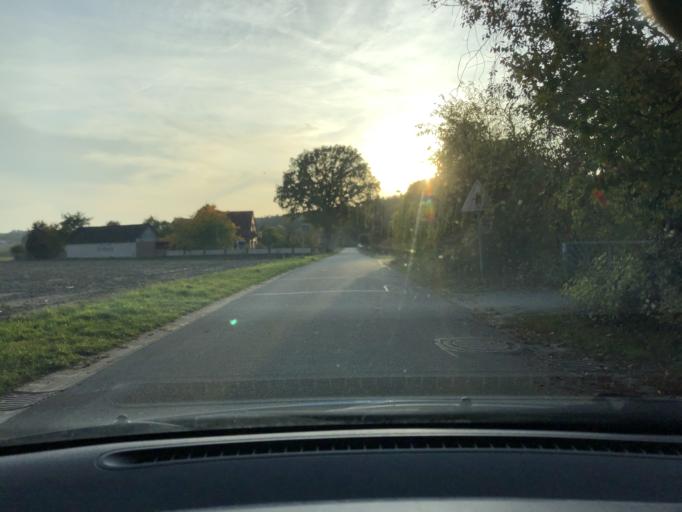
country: DE
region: Lower Saxony
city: Gohrde
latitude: 53.1356
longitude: 10.9513
